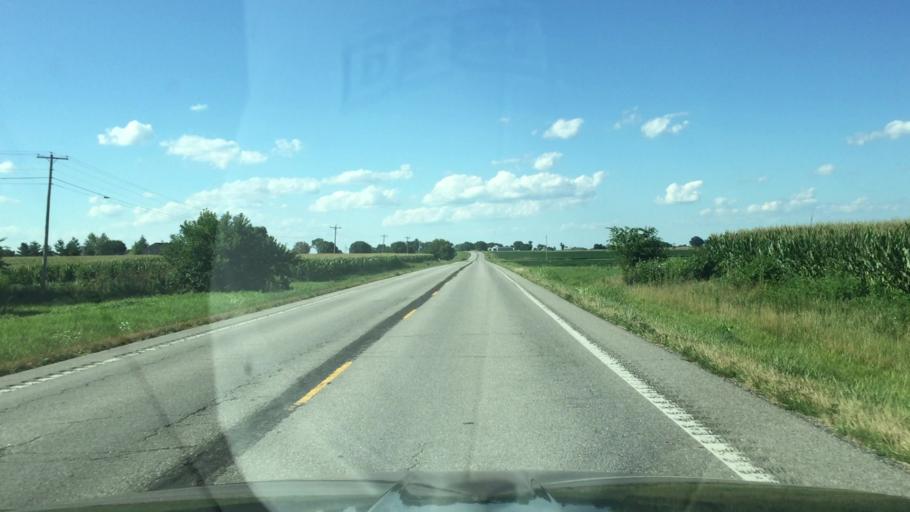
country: US
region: Missouri
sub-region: Moniteau County
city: Tipton
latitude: 38.5957
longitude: -92.7892
